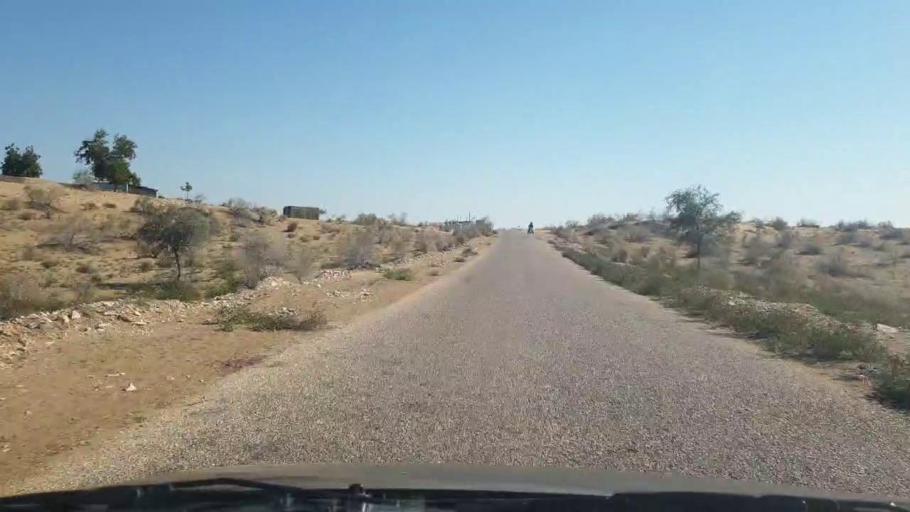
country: PK
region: Sindh
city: Bozdar
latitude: 27.0145
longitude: 68.7842
